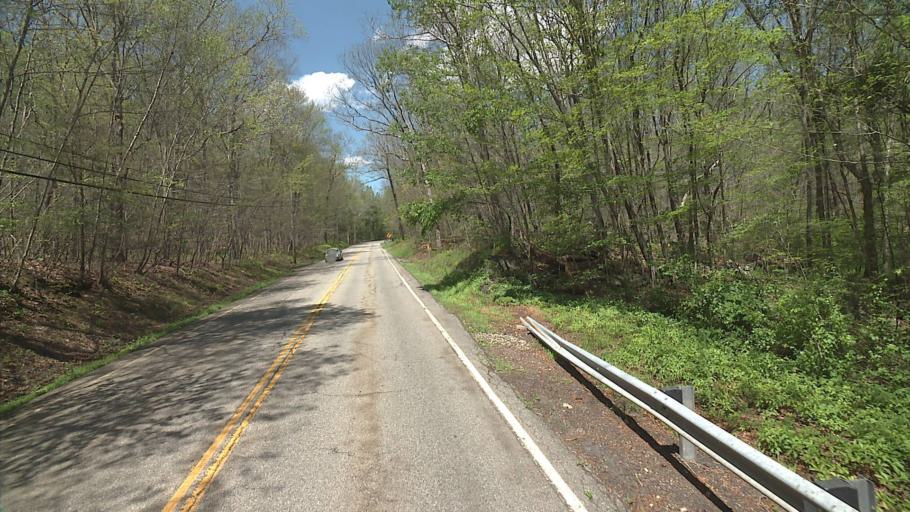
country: US
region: Connecticut
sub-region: Middlesex County
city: Moodus
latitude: 41.5217
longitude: -72.4887
